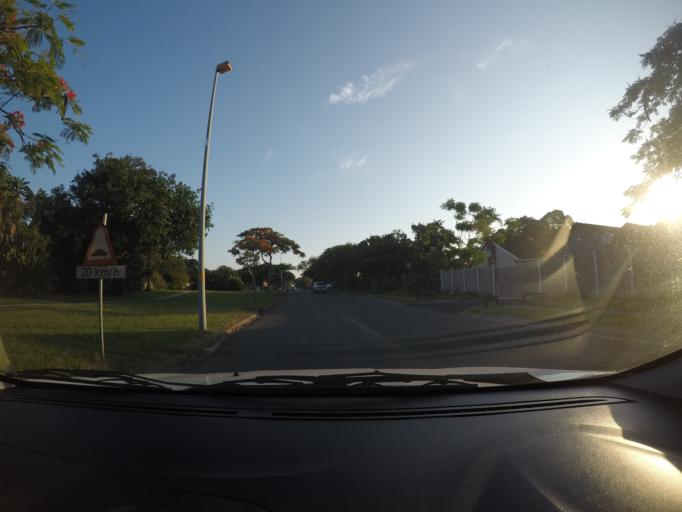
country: ZA
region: KwaZulu-Natal
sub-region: uThungulu District Municipality
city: Richards Bay
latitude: -28.7803
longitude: 32.0996
